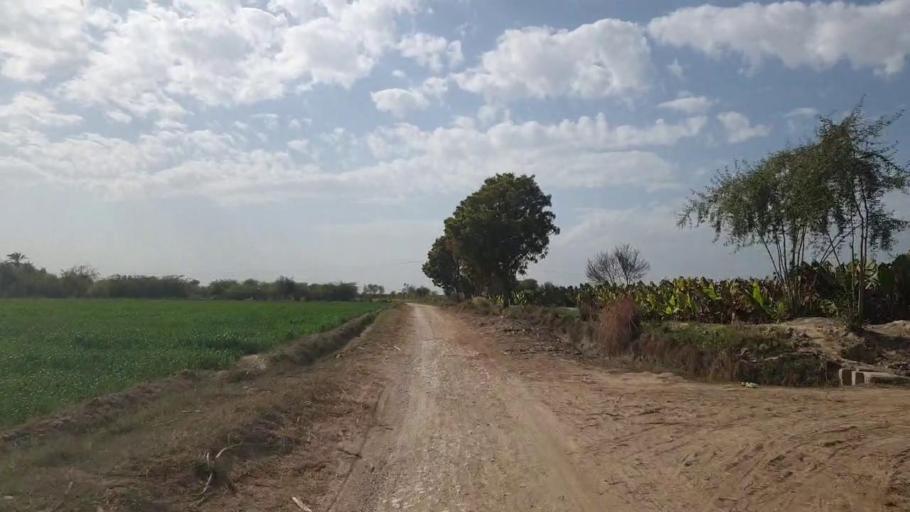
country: PK
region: Sindh
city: Shahdadpur
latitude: 25.9873
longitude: 68.4767
